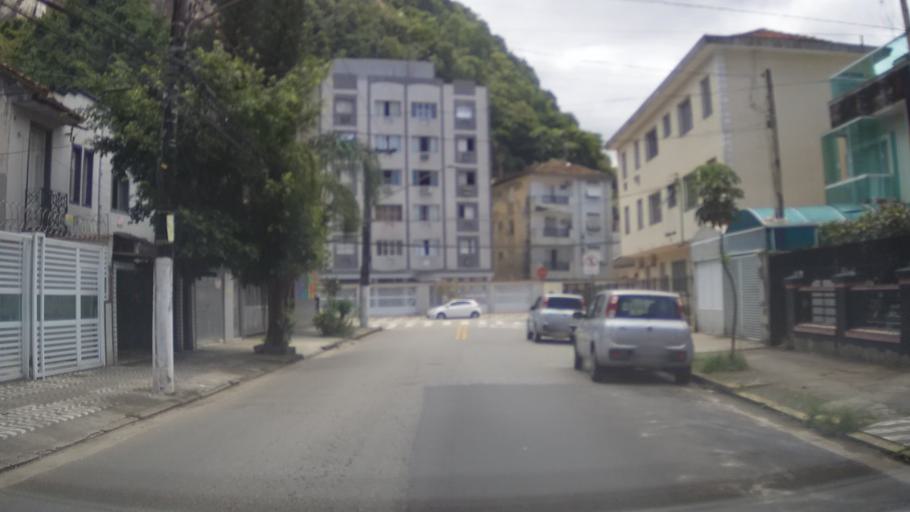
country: BR
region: Sao Paulo
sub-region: Santos
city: Santos
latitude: -23.9633
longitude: -46.3498
